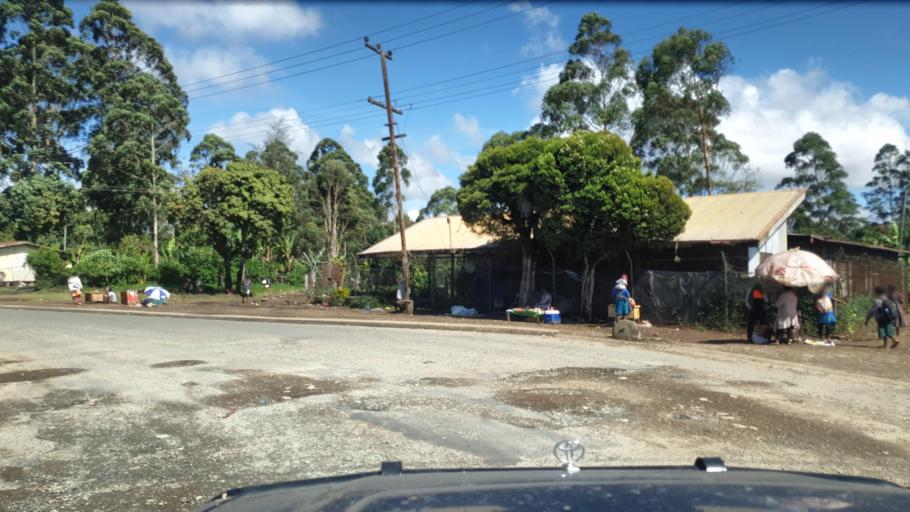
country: PG
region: Western Highlands
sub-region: Hagen
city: Mount Hagen
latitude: -5.8529
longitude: 144.2348
